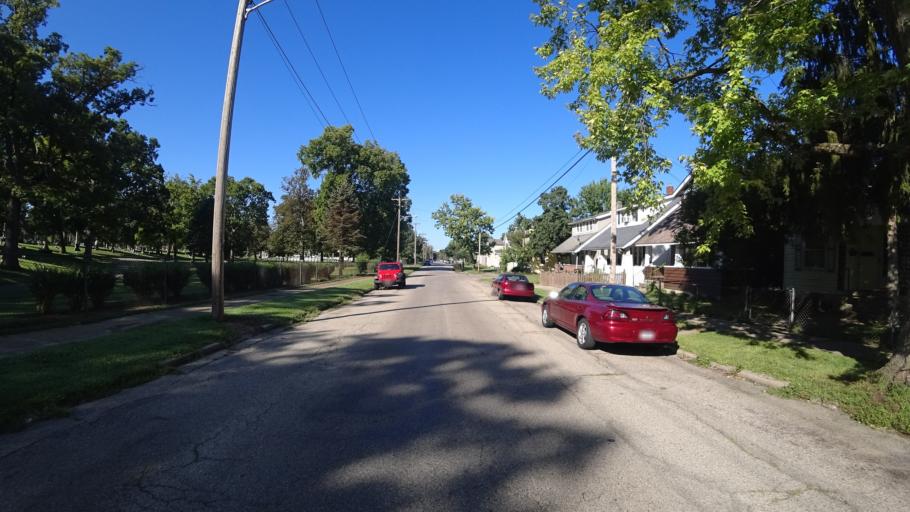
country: US
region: Ohio
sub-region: Butler County
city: Hamilton
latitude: 39.4047
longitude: -84.5444
